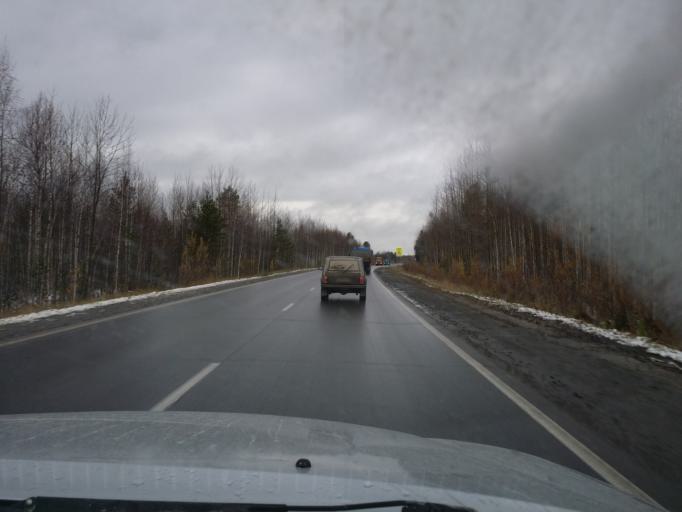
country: RU
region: Khanty-Mansiyskiy Avtonomnyy Okrug
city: Megion
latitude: 61.1284
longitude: 75.7921
